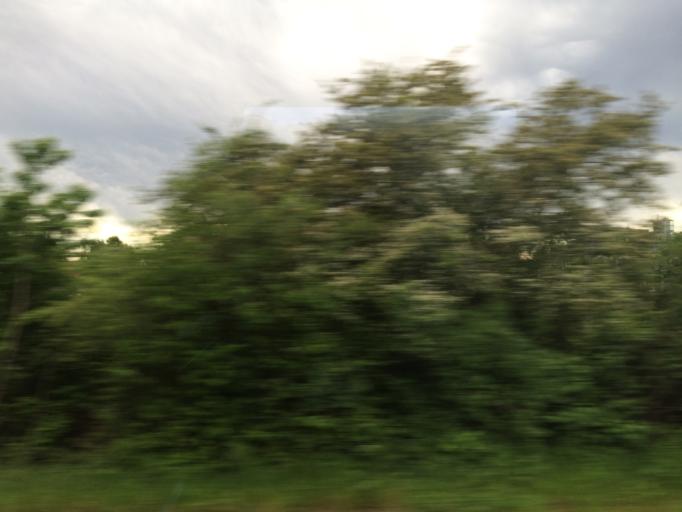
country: DE
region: Bavaria
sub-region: Regierungsbezirk Unterfranken
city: Mainaschaff
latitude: 49.9890
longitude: 9.0857
